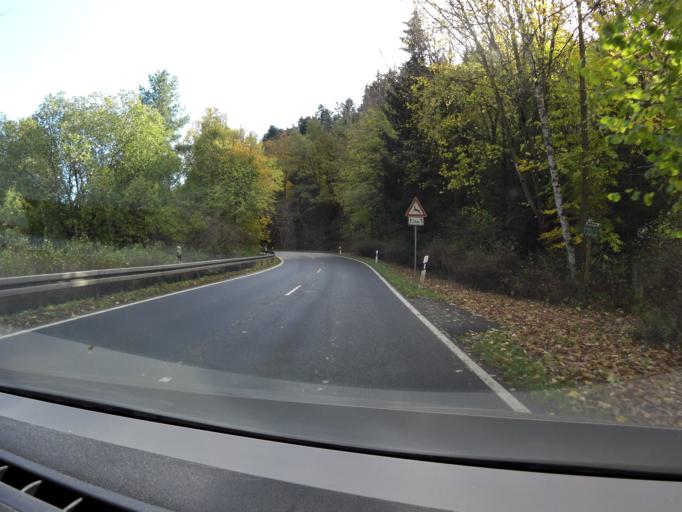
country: DE
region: Thuringia
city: Elgersburg
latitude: 50.7028
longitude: 10.8662
